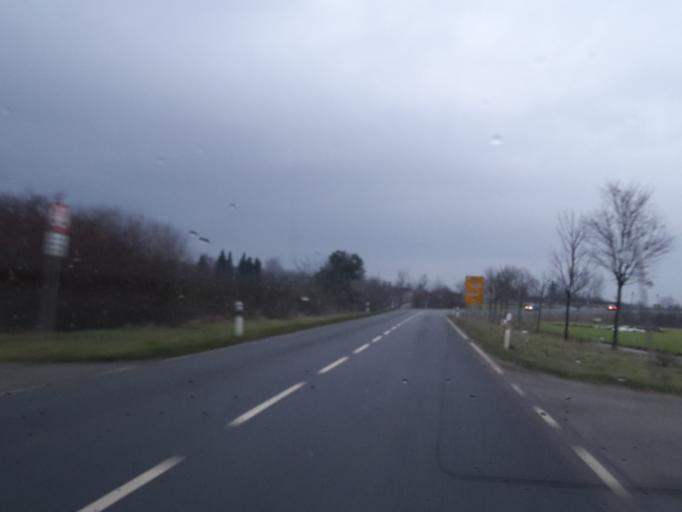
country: DE
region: Hesse
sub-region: Regierungsbezirk Darmstadt
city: Buttelborn
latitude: 49.9154
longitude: 8.5257
